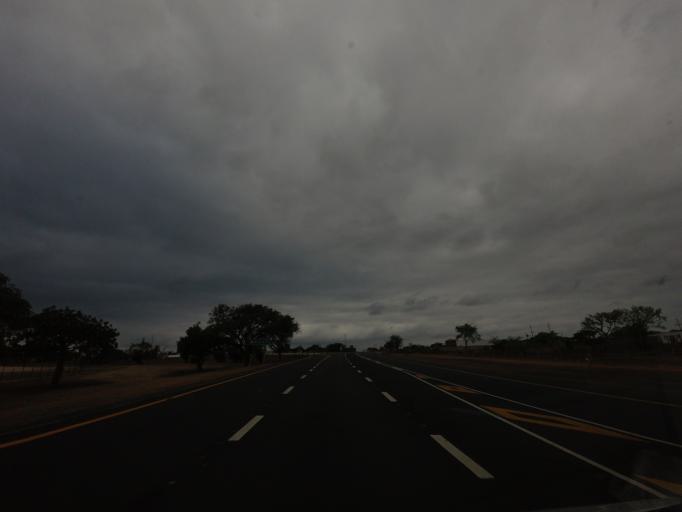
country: ZA
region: Mpumalanga
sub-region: Ehlanzeni District
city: Komatipoort
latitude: -25.4445
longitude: 31.6786
